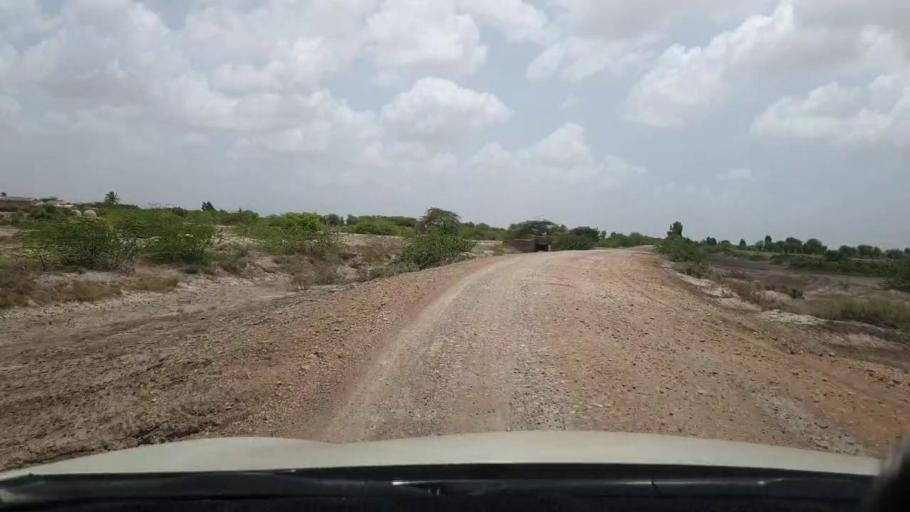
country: PK
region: Sindh
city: Kadhan
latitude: 24.3787
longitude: 68.9296
